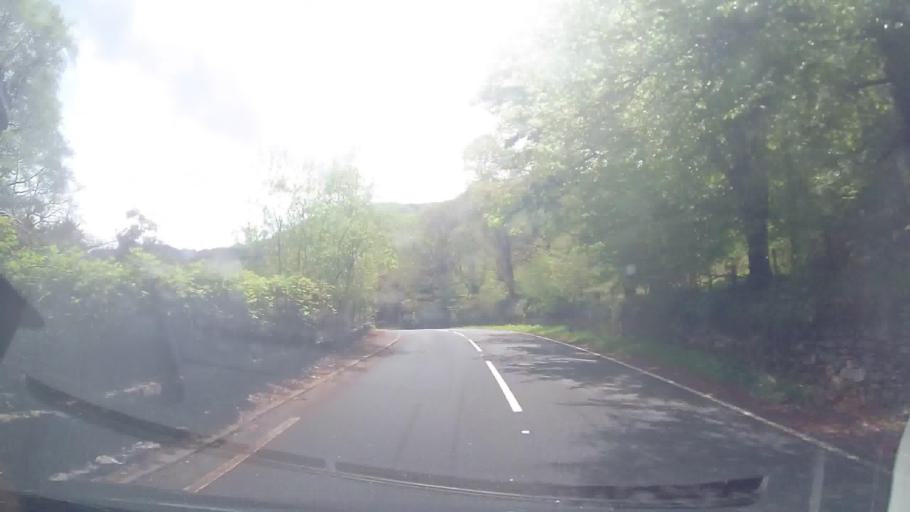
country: GB
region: Wales
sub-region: Gwynedd
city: Penrhyndeudraeth
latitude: 53.0104
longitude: -4.1040
